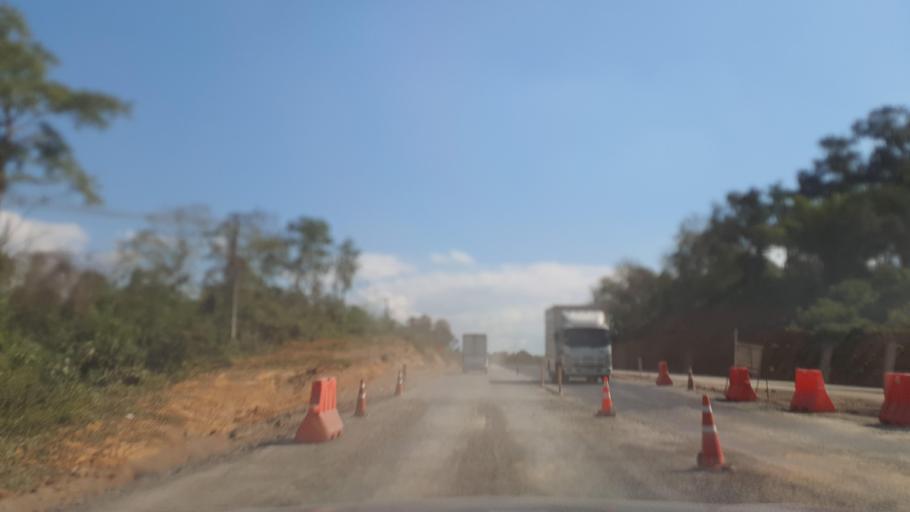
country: TH
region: Nan
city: Nan
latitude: 18.8274
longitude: 100.7620
